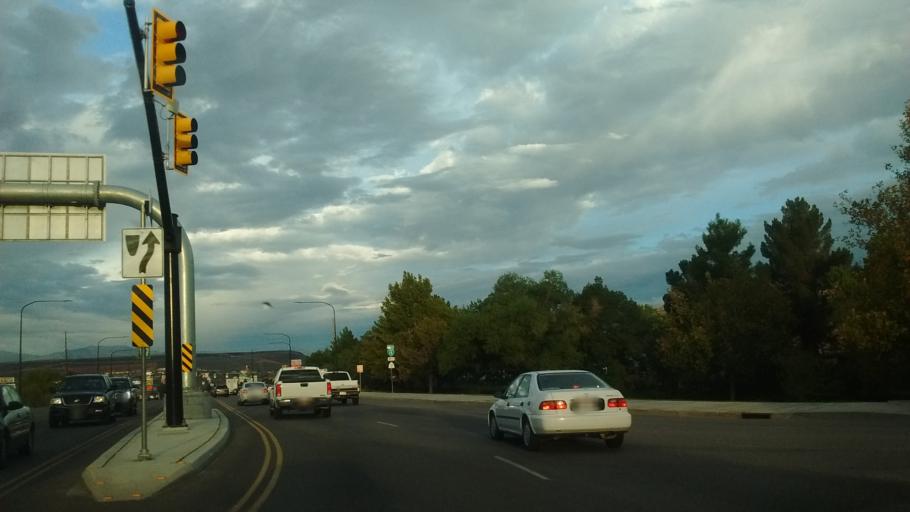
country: US
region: Utah
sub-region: Washington County
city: Saint George
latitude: 37.1099
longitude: -113.5596
